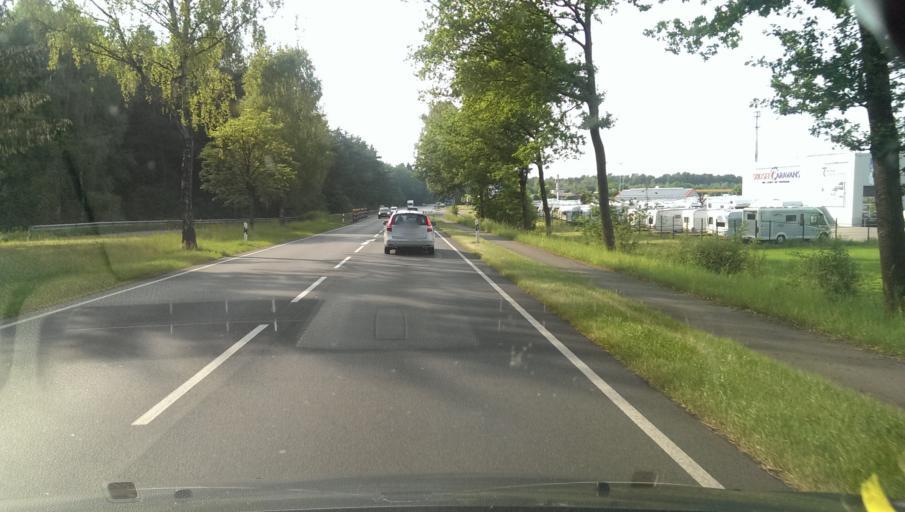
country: DE
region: Lower Saxony
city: Soltau
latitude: 52.9429
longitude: 9.8829
